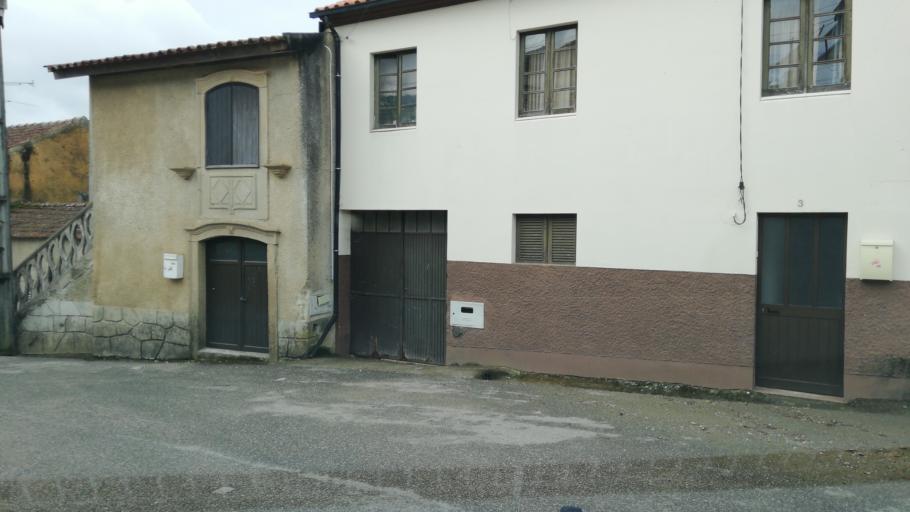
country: PT
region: Aveiro
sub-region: Agueda
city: Valongo
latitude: 40.6193
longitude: -8.4244
